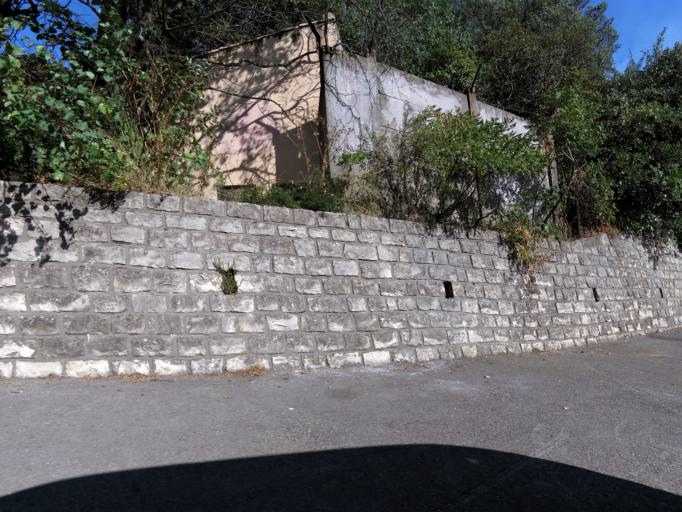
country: FR
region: Languedoc-Roussillon
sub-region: Departement du Gard
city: Nimes
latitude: 43.8414
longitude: 4.3413
